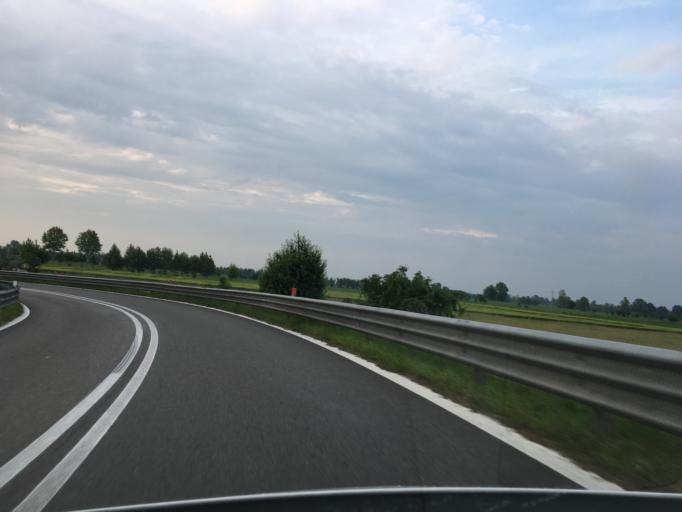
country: IT
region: Lombardy
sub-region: Provincia di Brescia
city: Alfianello
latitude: 45.2723
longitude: 10.1314
